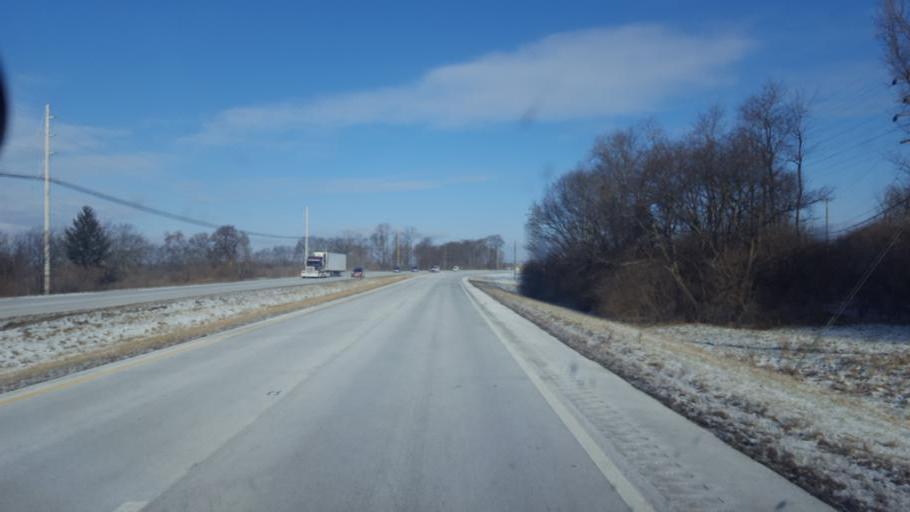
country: US
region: Ohio
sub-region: Franklin County
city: Obetz
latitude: 39.8216
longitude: -83.0005
